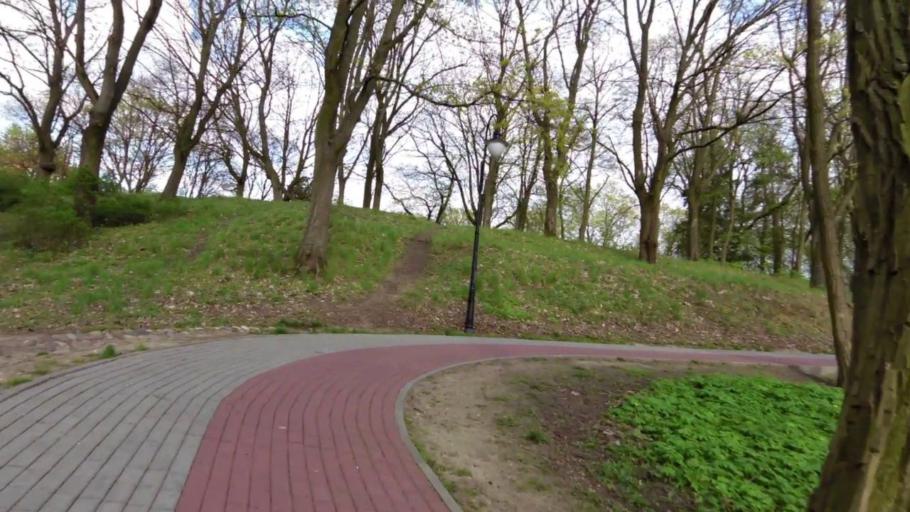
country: PL
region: West Pomeranian Voivodeship
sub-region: Powiat mysliborski
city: Barlinek
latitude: 52.9887
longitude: 15.2153
